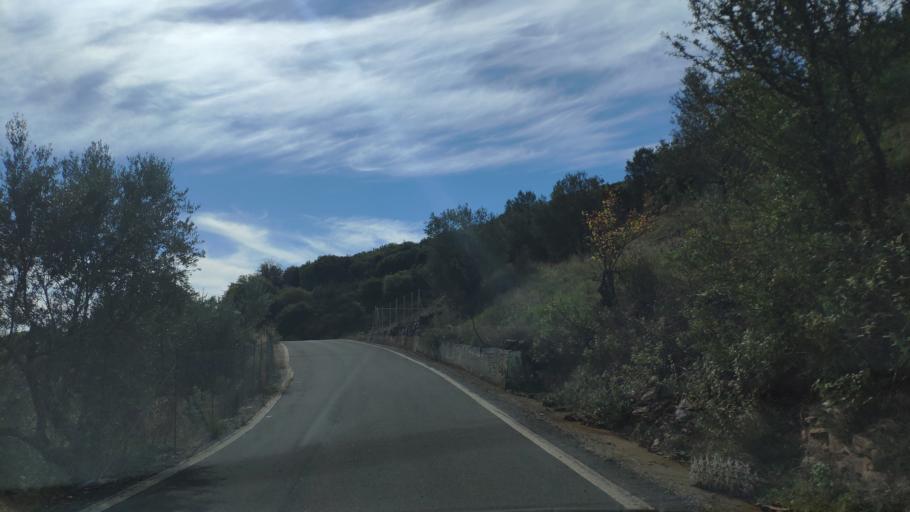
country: GR
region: Peloponnese
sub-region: Nomos Arkadias
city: Dimitsana
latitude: 37.5257
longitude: 22.0707
